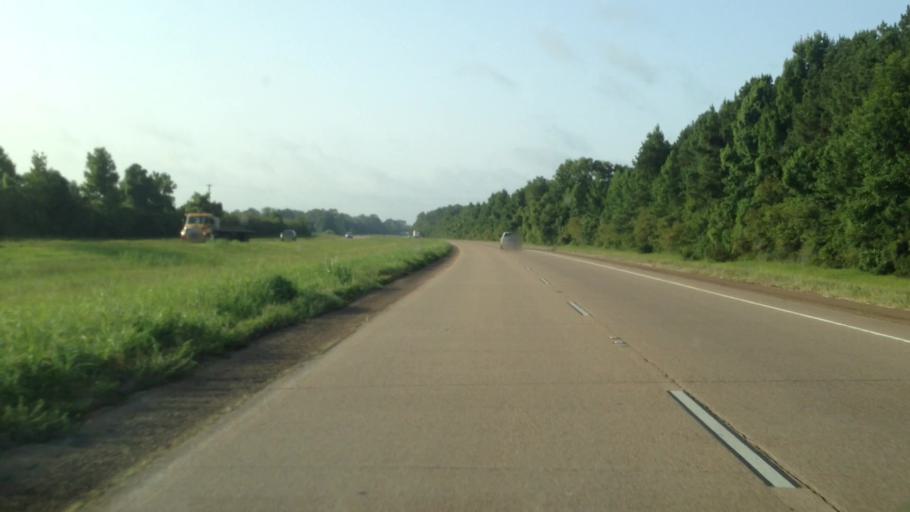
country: US
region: Louisiana
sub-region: Rapides Parish
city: Woodworth
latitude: 31.1402
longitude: -92.4511
